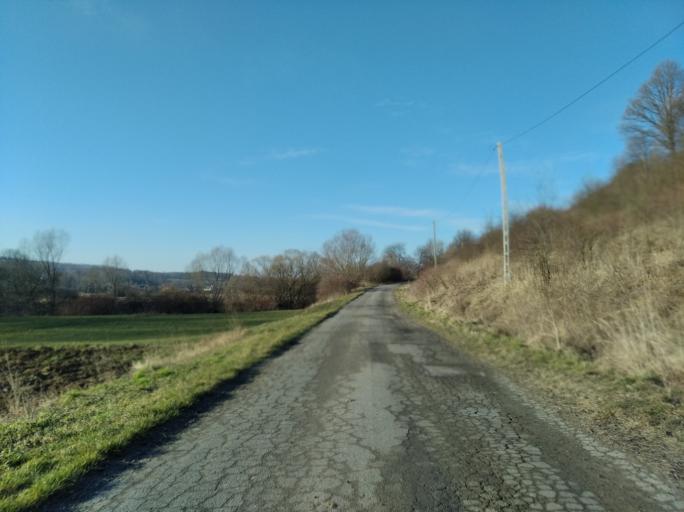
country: PL
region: Subcarpathian Voivodeship
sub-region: Powiat strzyzowski
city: Strzyzow
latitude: 49.8262
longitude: 21.8337
